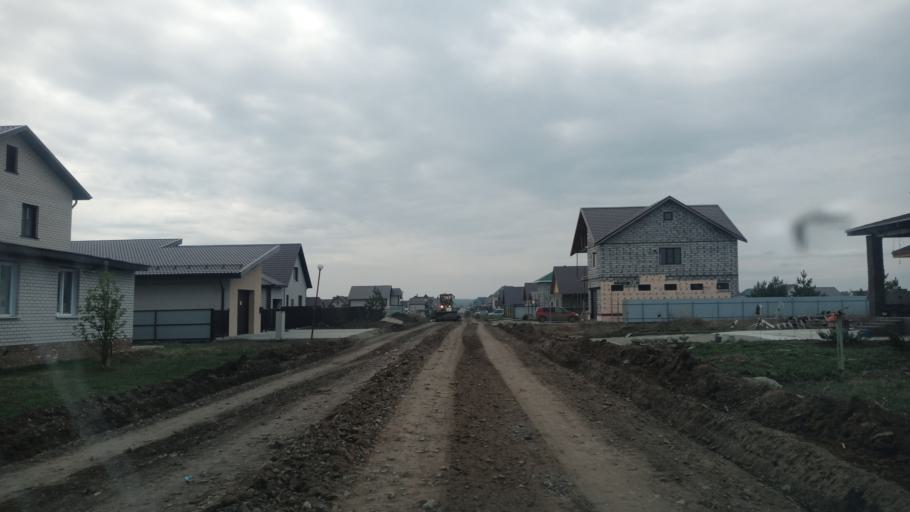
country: RU
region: Altai Krai
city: Yuzhnyy
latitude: 53.2278
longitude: 83.6912
